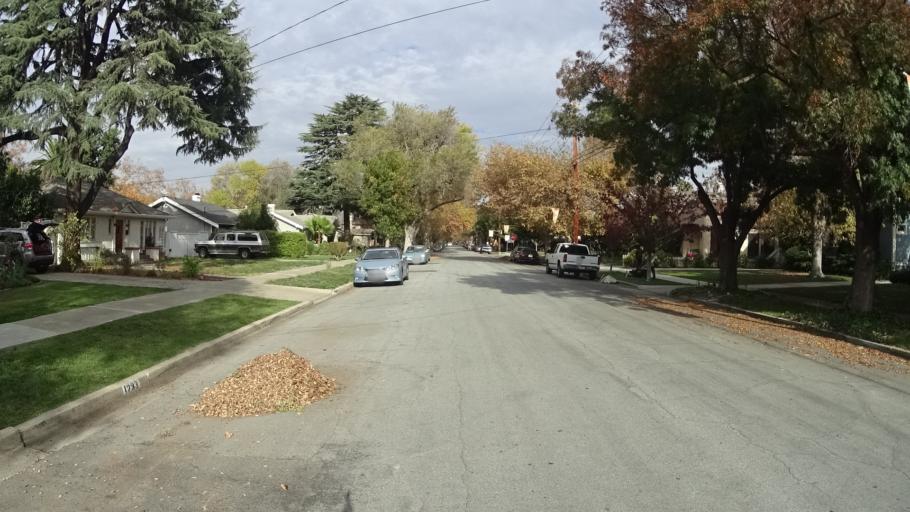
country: US
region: California
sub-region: Santa Clara County
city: Burbank
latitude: 37.3401
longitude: -121.9264
